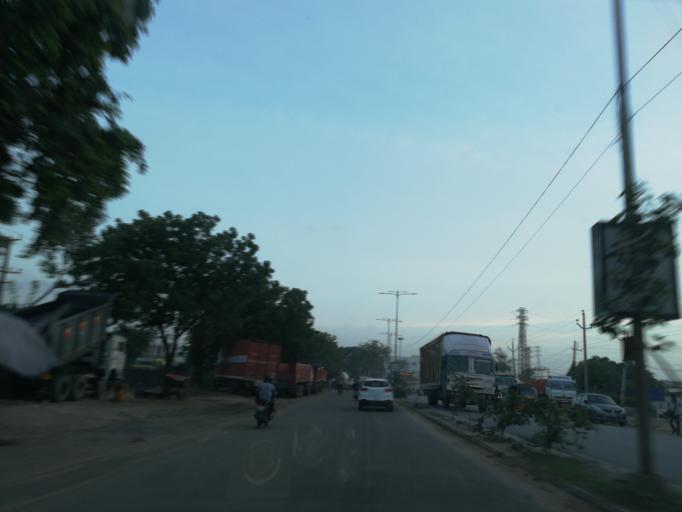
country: IN
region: Telangana
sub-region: Medak
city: Serilingampalle
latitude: 17.5356
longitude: 78.3581
